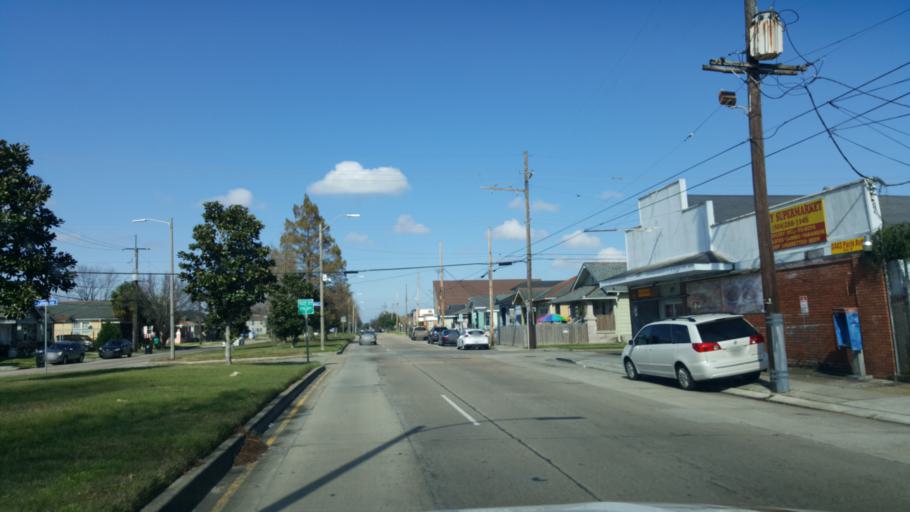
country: US
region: Louisiana
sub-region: Orleans Parish
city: New Orleans
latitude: 29.9926
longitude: -90.0731
